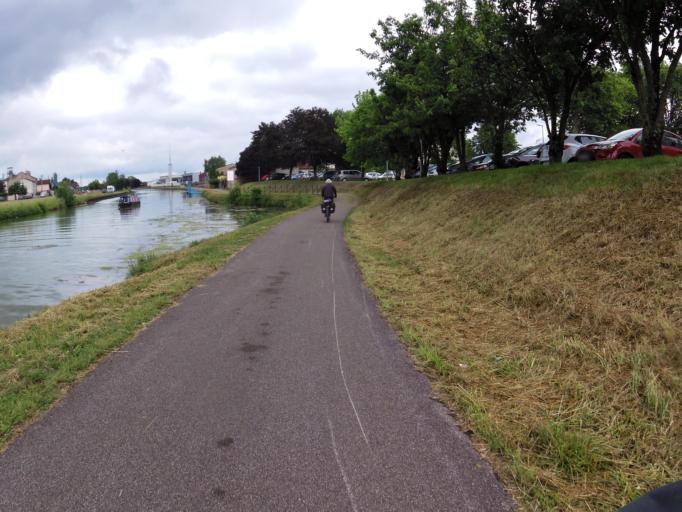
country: FR
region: Champagne-Ardenne
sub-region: Departement de la Haute-Marne
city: Saint-Dizier
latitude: 48.6414
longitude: 4.9483
